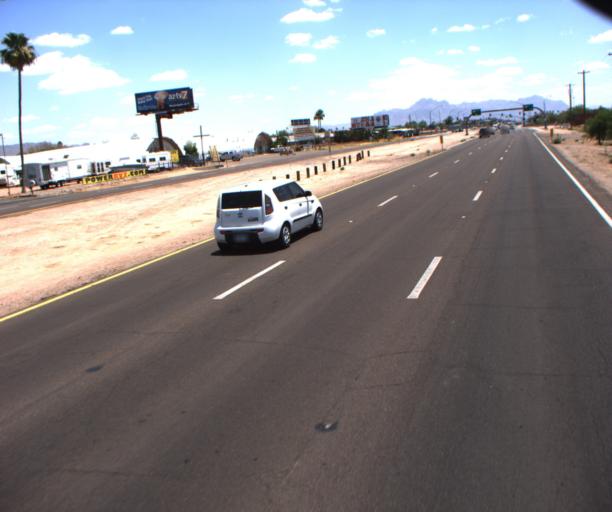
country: US
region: Arizona
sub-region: Pinal County
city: Apache Junction
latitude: 33.4151
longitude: -111.6408
